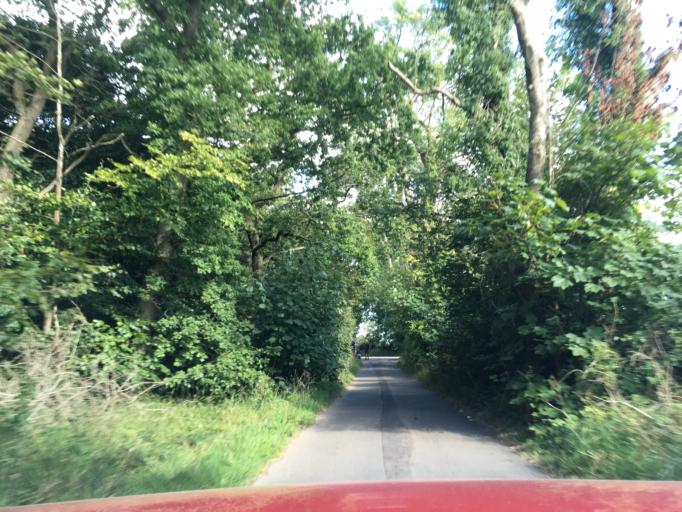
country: GB
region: England
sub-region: Gloucestershire
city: Painswick
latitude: 51.7766
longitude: -2.2400
